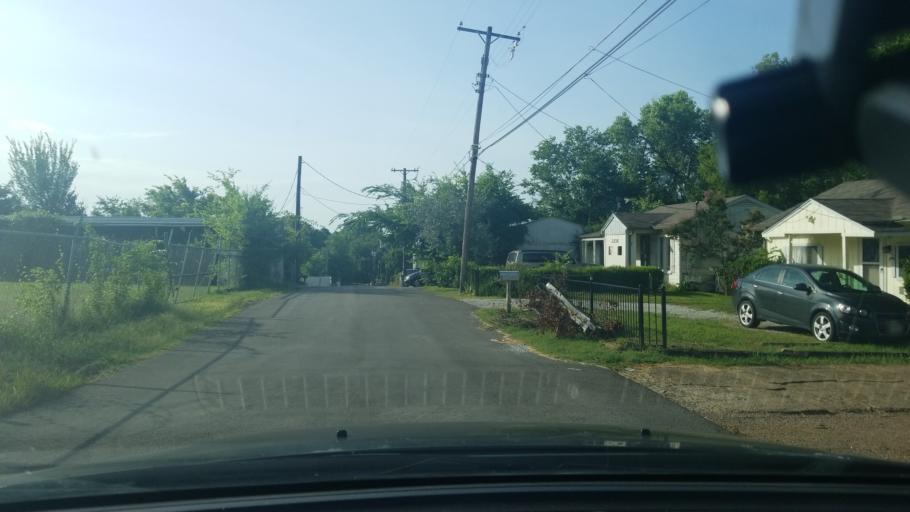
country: US
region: Texas
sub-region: Dallas County
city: Highland Park
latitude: 32.7984
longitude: -96.7160
